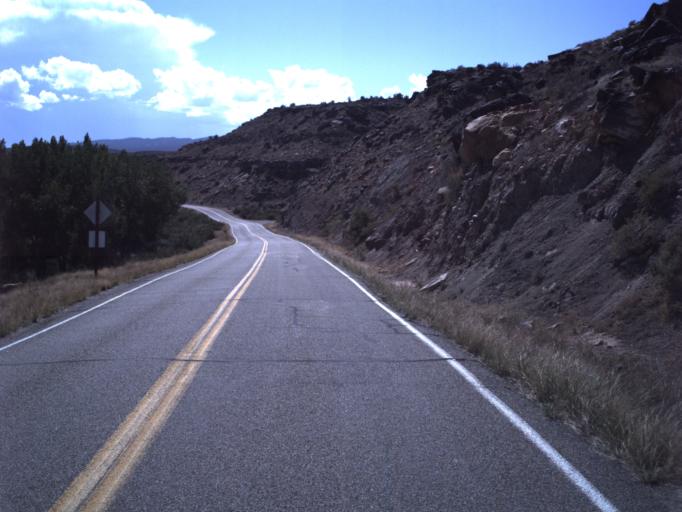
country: US
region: Utah
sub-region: Grand County
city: Moab
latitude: 38.8315
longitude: -109.2872
